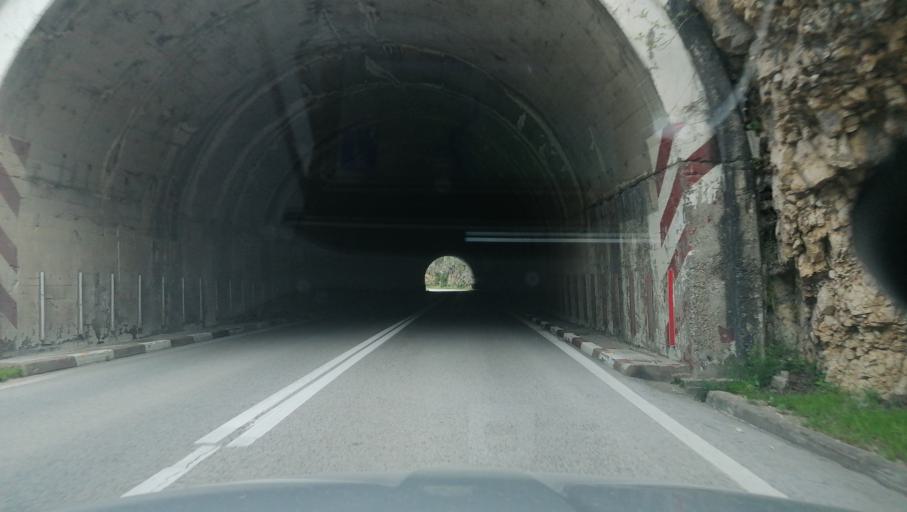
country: BA
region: Republika Srpska
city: Mrkonjic Grad
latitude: 44.4630
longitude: 17.1837
